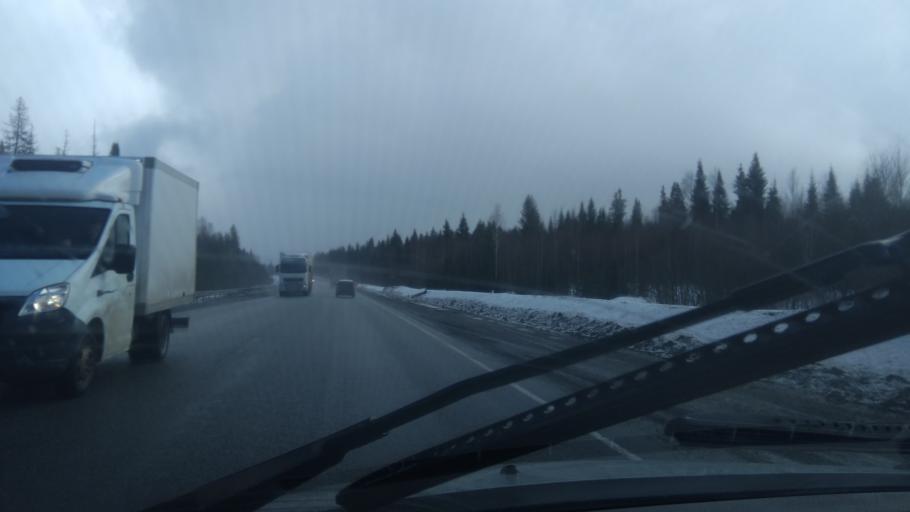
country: RU
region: Sverdlovsk
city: Arti
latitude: 56.7890
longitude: 58.5050
